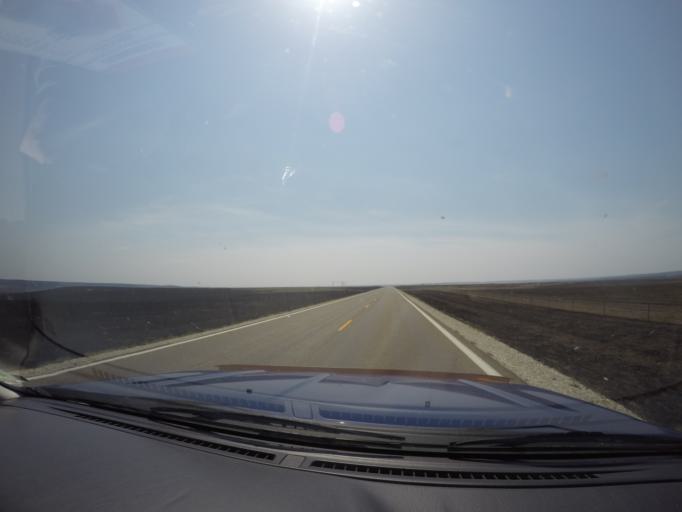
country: US
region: Kansas
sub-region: Chase County
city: Cottonwood Falls
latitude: 38.5084
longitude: -96.5472
